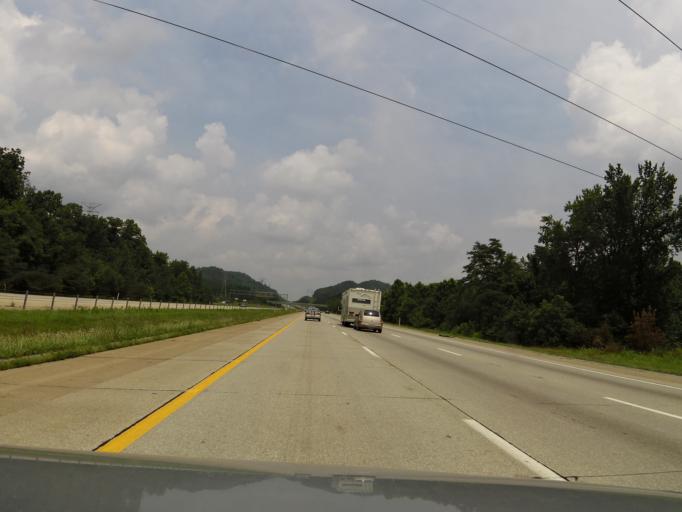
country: US
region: Kentucky
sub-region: Bullitt County
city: Lebanon Junction
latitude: 37.8667
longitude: -85.7052
